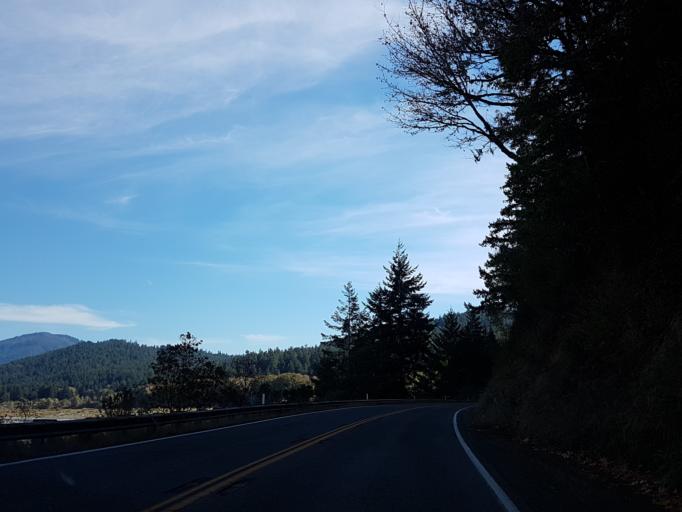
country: US
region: California
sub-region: Humboldt County
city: Rio Dell
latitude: 40.4260
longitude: -123.9808
